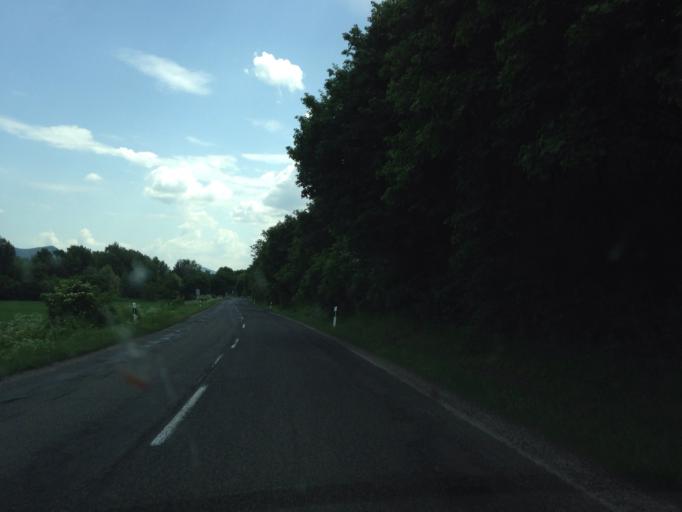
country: HU
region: Pest
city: Szob
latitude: 47.8036
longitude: 18.8506
